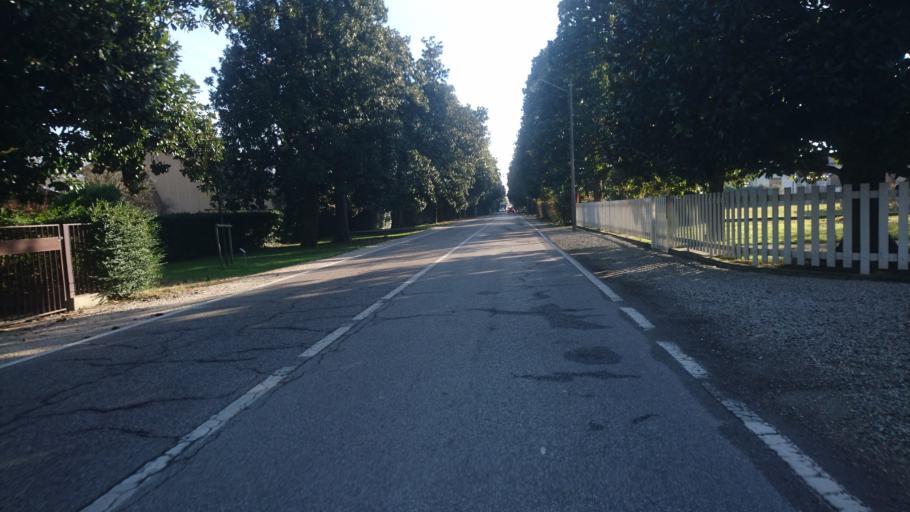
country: IT
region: Veneto
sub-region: Provincia di Padova
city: Piazzola sul Brenta
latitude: 45.5396
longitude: 11.7875
